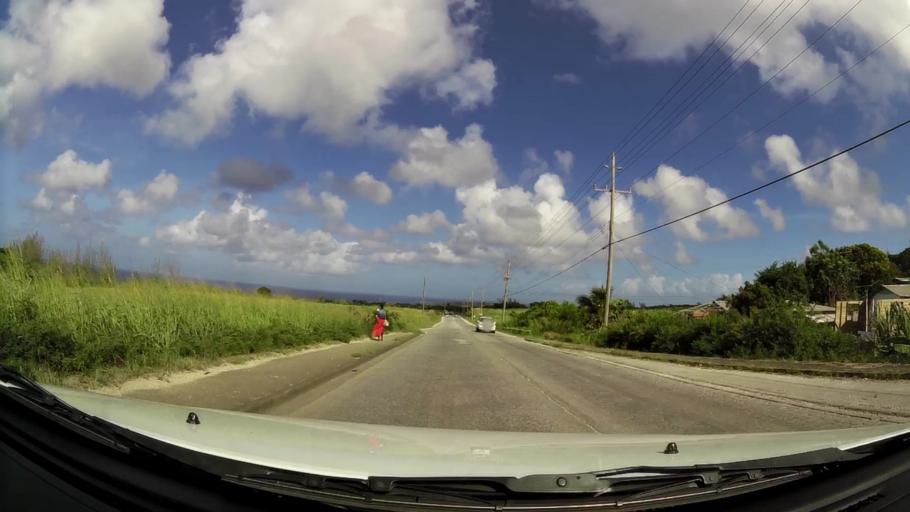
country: BB
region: Saint Peter
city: Speightstown
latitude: 13.2380
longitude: -59.6239
